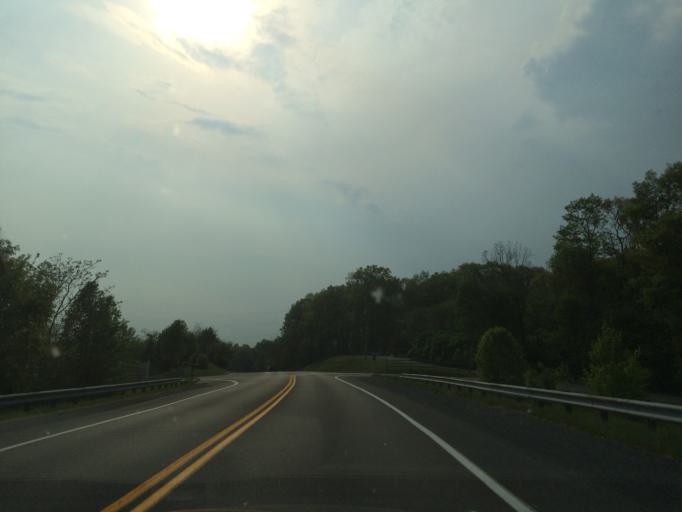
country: US
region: Maryland
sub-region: Carroll County
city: Mount Airy
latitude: 39.3550
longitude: -77.1225
